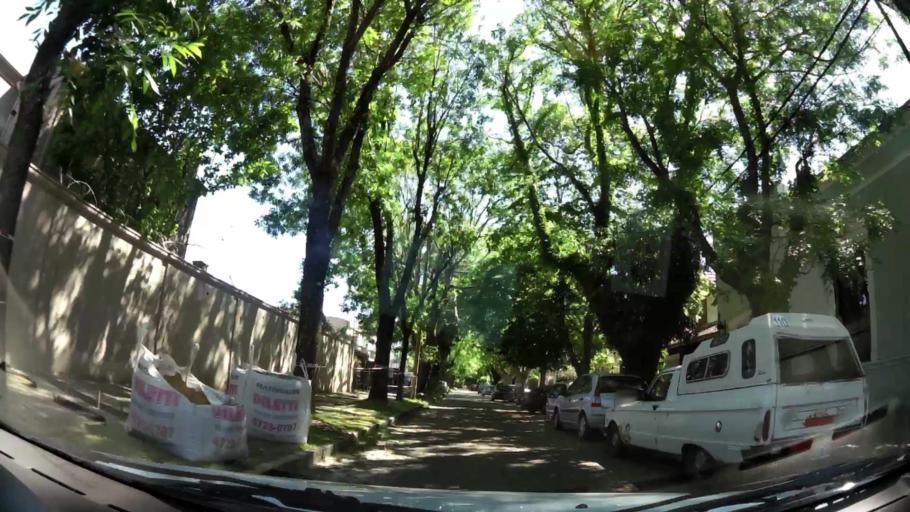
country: AR
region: Buenos Aires
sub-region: Partido de San Isidro
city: San Isidro
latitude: -34.4823
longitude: -58.4961
